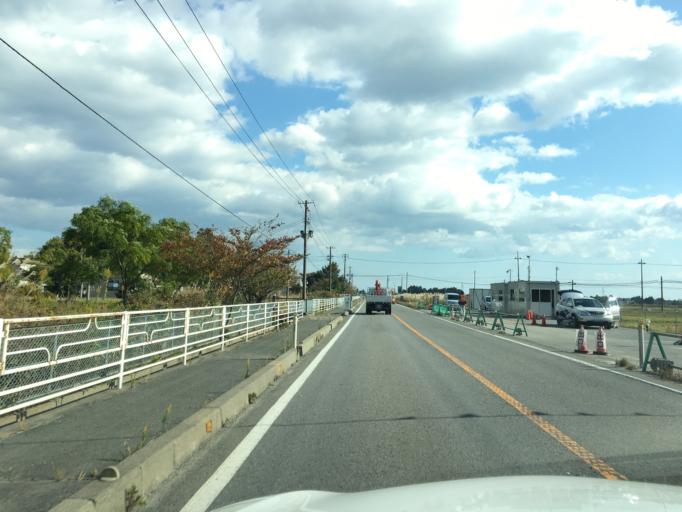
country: JP
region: Fukushima
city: Namie
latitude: 37.3691
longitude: 140.9782
